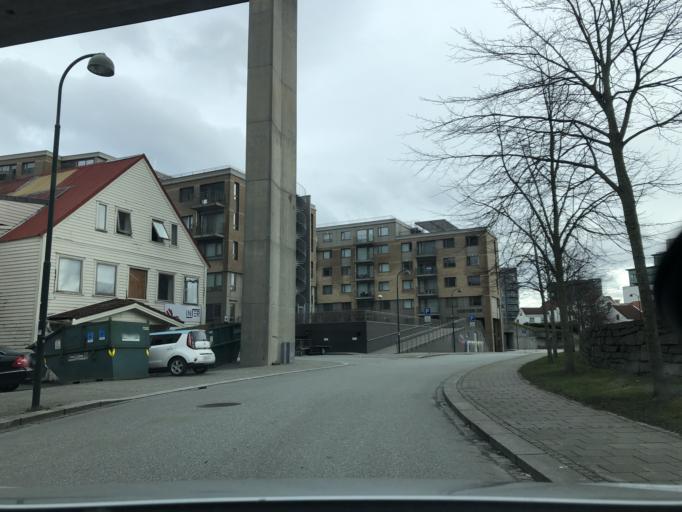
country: NO
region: Rogaland
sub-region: Stavanger
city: Stavanger
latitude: 58.9725
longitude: 5.7477
